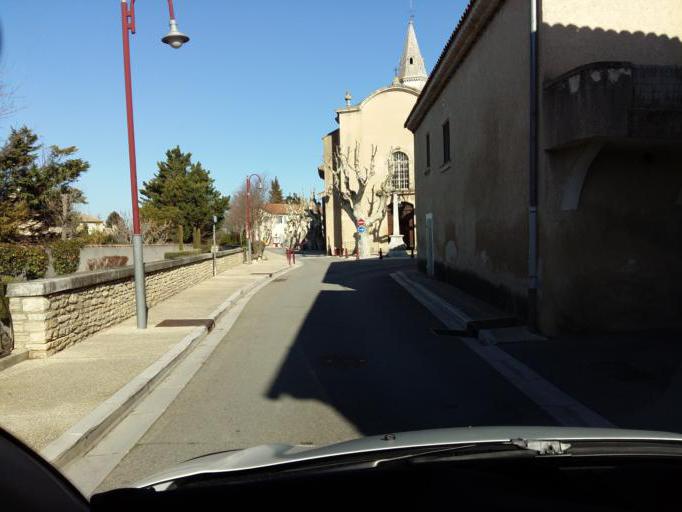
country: FR
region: Provence-Alpes-Cote d'Azur
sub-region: Departement du Vaucluse
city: Cheval-Blanc
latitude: 43.8001
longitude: 5.0628
